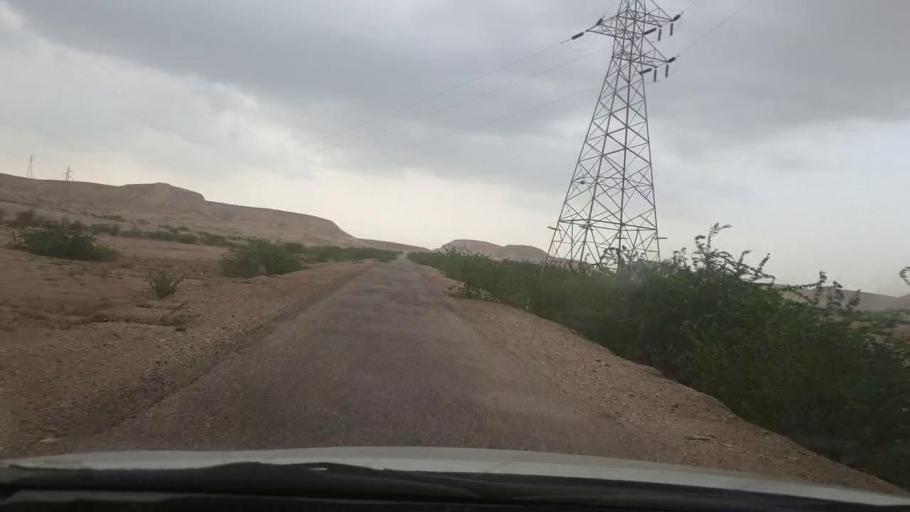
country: PK
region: Sindh
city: Khairpur
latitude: 27.4669
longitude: 68.9214
